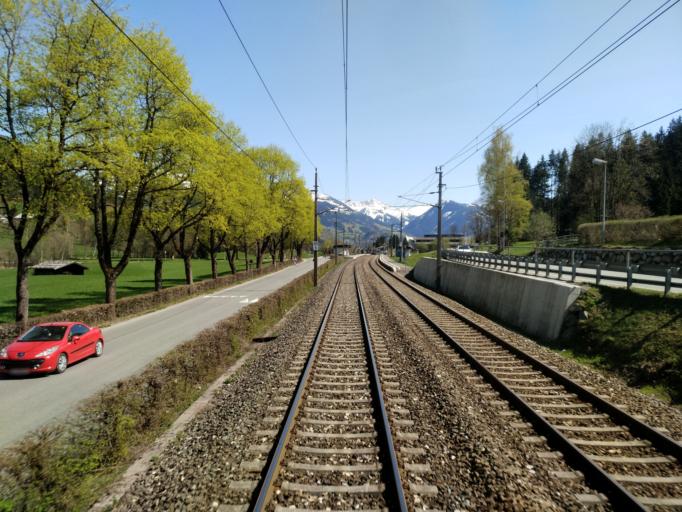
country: AT
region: Tyrol
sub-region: Politischer Bezirk Kitzbuhel
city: Reith bei Kitzbuhel
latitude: 47.4543
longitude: 12.3685
